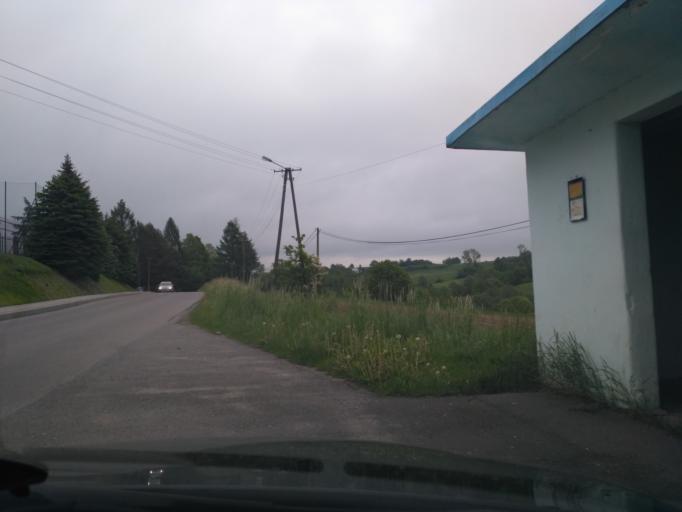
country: PL
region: Subcarpathian Voivodeship
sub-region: Powiat ropczycko-sedziszowski
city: Niedzwiada
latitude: 49.9653
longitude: 21.5147
